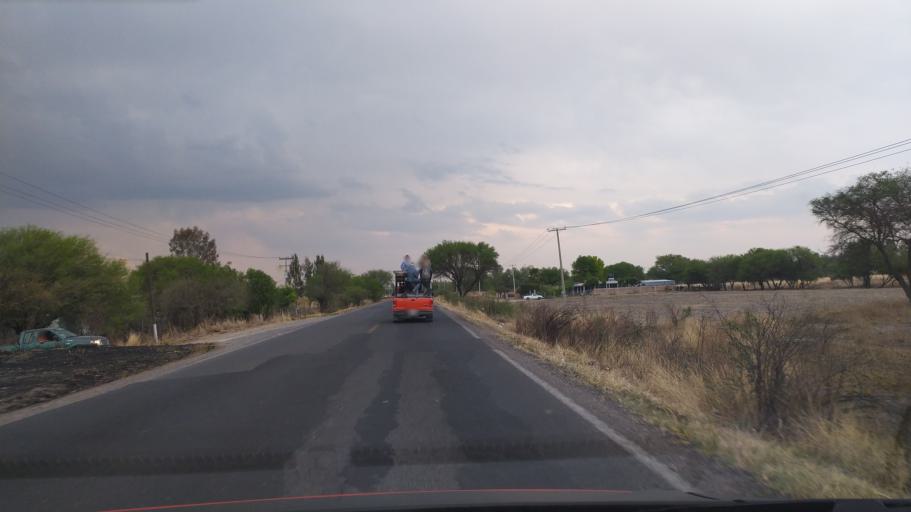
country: MX
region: Guanajuato
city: Ciudad Manuel Doblado
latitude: 20.7863
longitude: -101.9079
